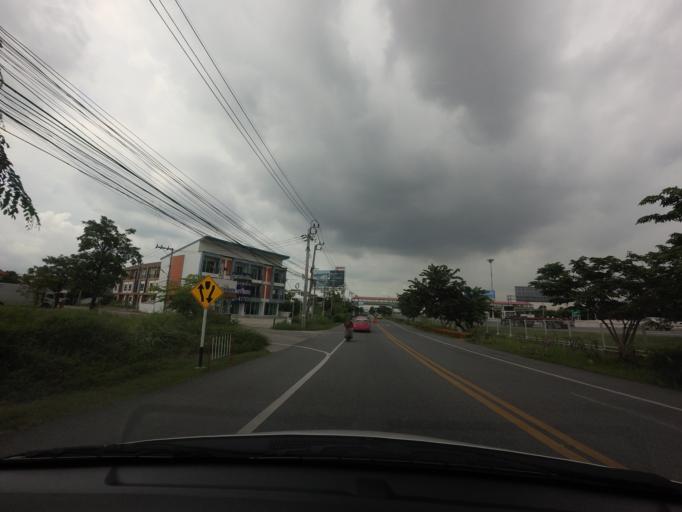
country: TH
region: Bangkok
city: Saphan Sung
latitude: 13.7671
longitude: 100.6926
